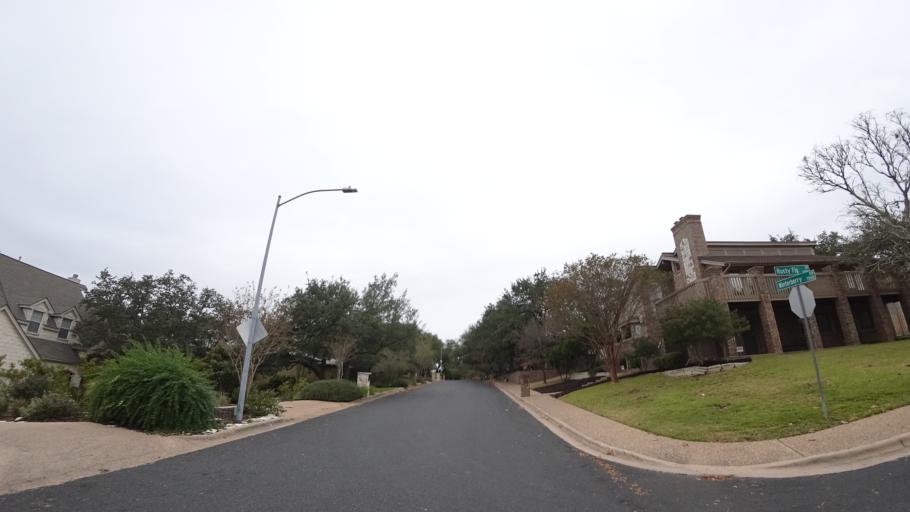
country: US
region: Texas
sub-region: Williamson County
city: Jollyville
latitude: 30.3742
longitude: -97.7971
